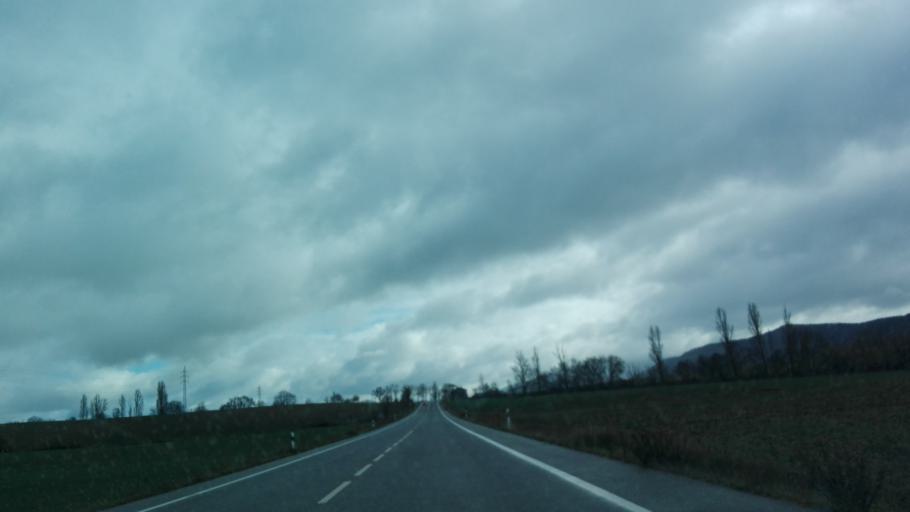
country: ES
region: Navarre
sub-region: Provincia de Navarra
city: Lizoain
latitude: 42.8155
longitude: -1.5086
